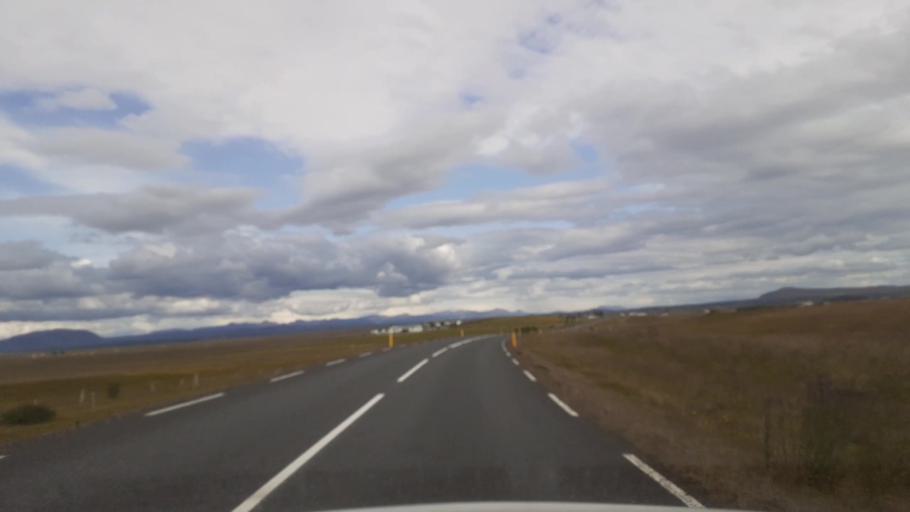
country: IS
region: South
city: Selfoss
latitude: 63.9252
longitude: -20.8518
